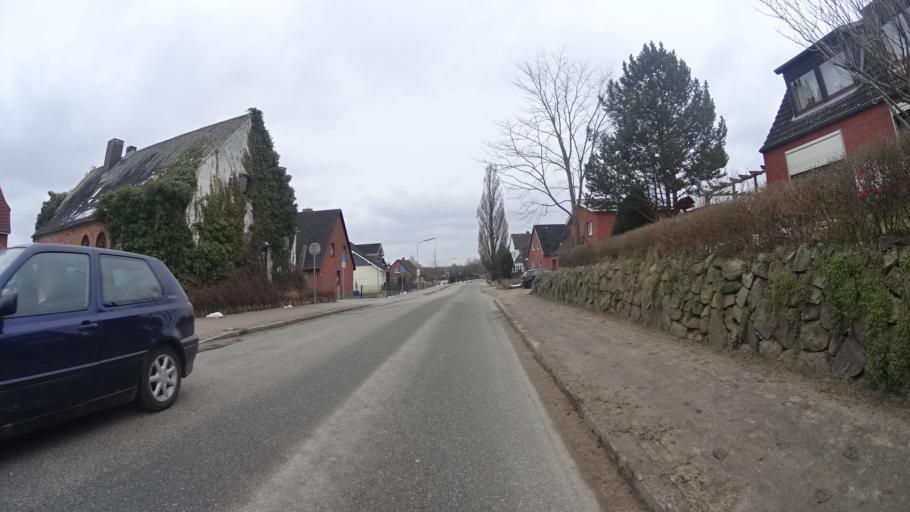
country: DE
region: Schleswig-Holstein
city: Neukirchen
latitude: 54.2022
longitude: 10.5604
